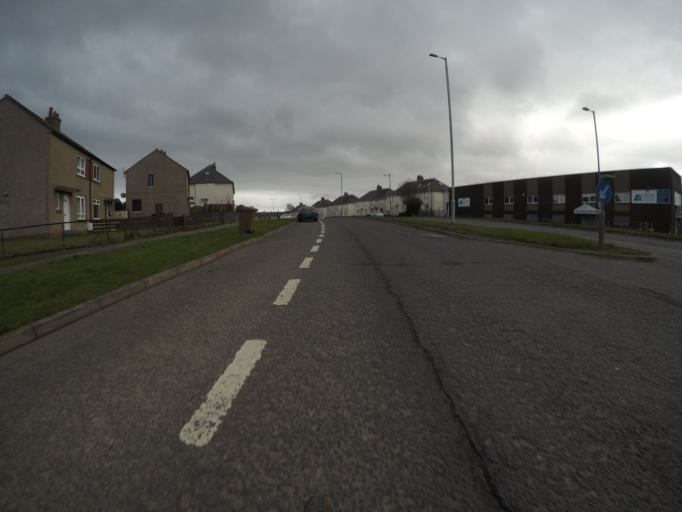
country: GB
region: Scotland
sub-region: East Ayrshire
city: Kilmarnock
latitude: 55.6149
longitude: -4.5139
